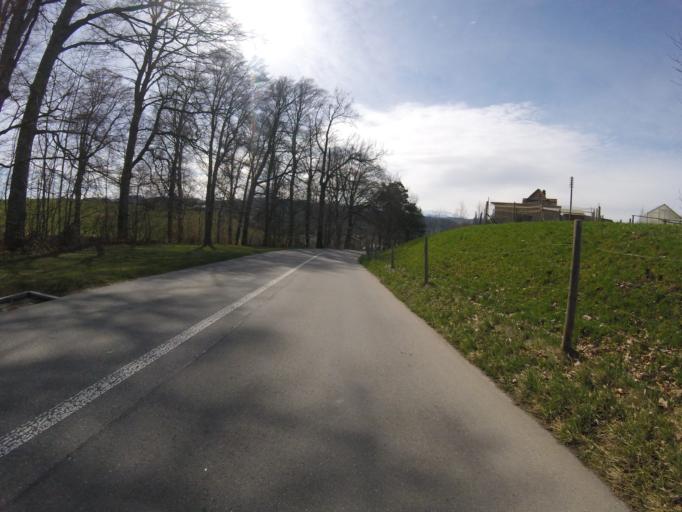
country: CH
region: Fribourg
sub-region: Sense District
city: Flamatt
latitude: 46.8978
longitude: 7.3082
